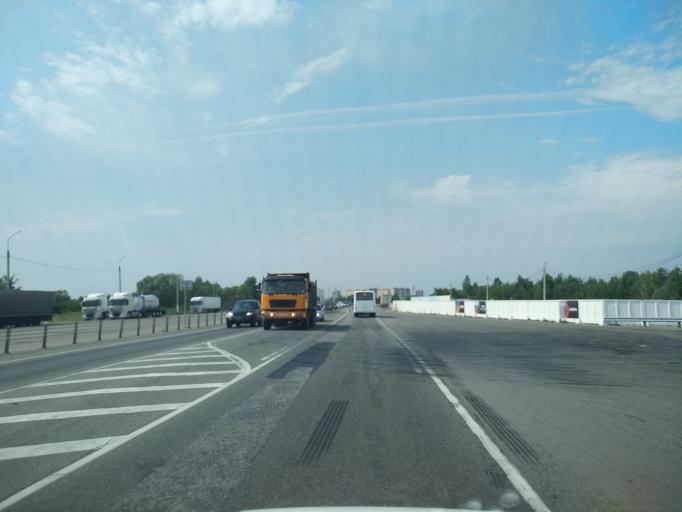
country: RU
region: Voronezj
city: Somovo
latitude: 51.6815
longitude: 39.3444
